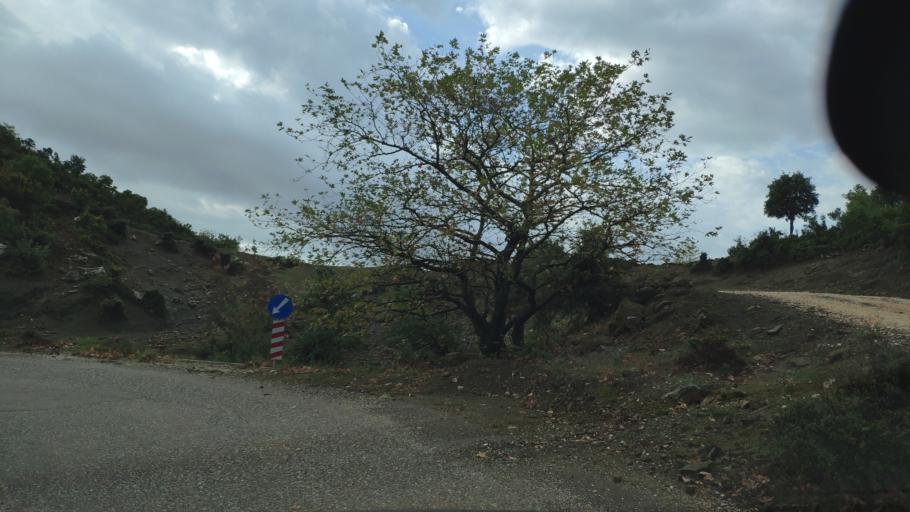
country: GR
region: West Greece
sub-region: Nomos Aitolias kai Akarnanias
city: Sardinia
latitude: 38.8539
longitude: 21.3068
